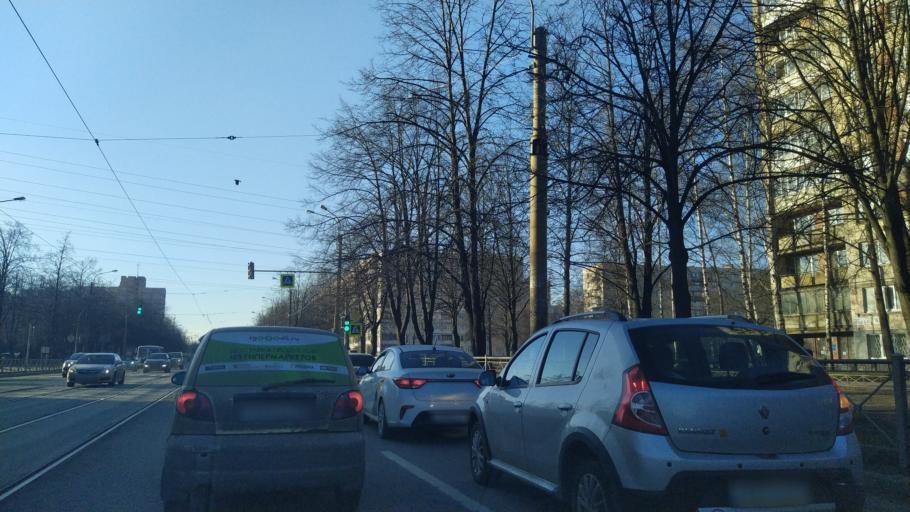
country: RU
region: Leningrad
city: Akademicheskoe
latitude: 60.0155
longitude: 30.3867
